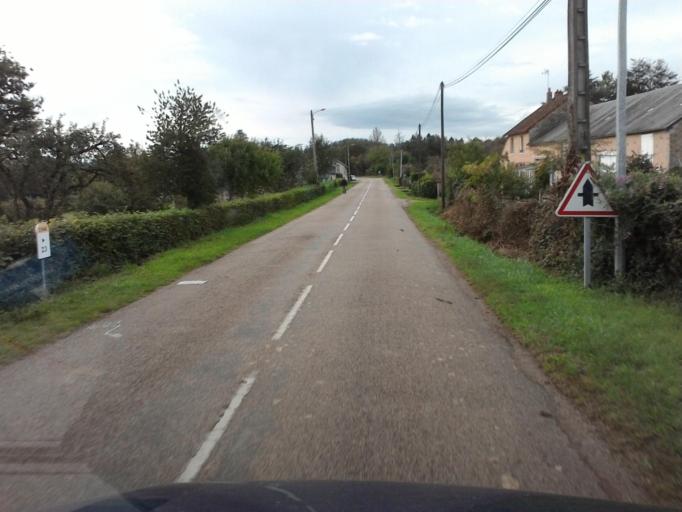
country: FR
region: Bourgogne
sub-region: Departement de la Nievre
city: Lormes
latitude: 47.2010
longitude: 3.8465
